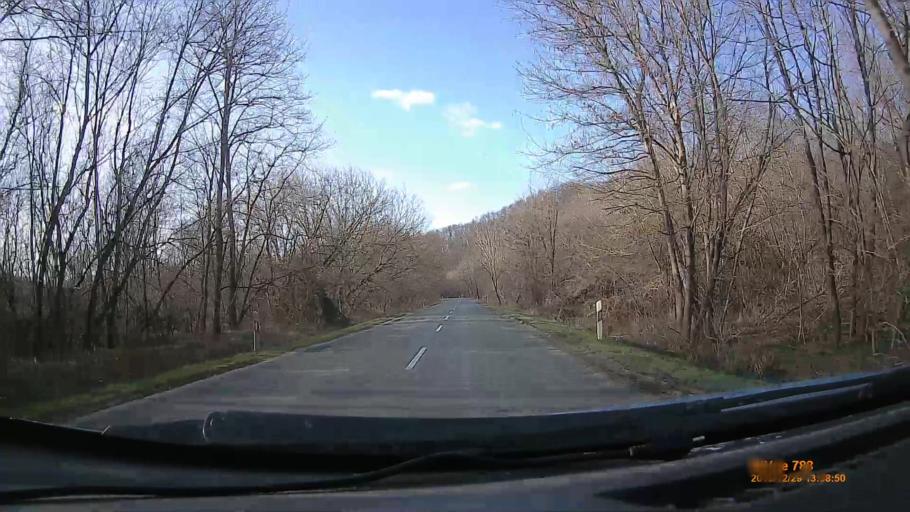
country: HU
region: Heves
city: Recsk
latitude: 47.9262
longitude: 20.1462
